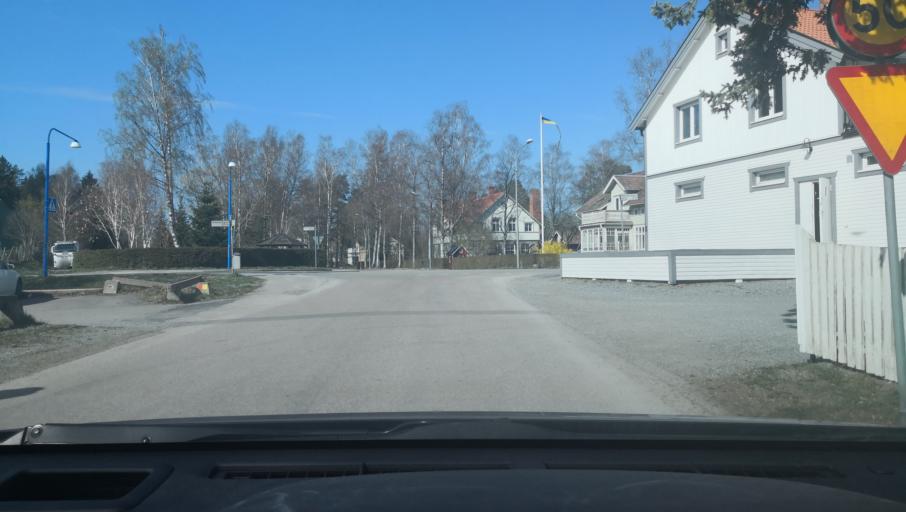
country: SE
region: Uppsala
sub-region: Enkopings Kommun
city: Irsta
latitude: 59.7765
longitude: 16.9281
